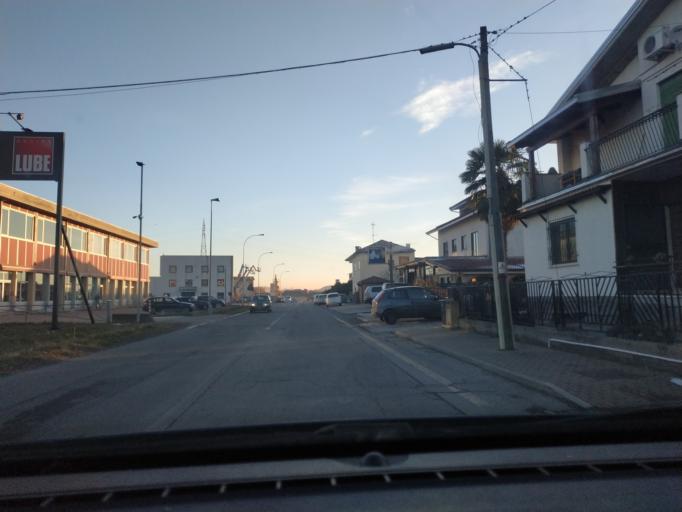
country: IT
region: Piedmont
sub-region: Provincia di Torino
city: Romano Canavese
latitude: 45.4248
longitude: 7.8827
